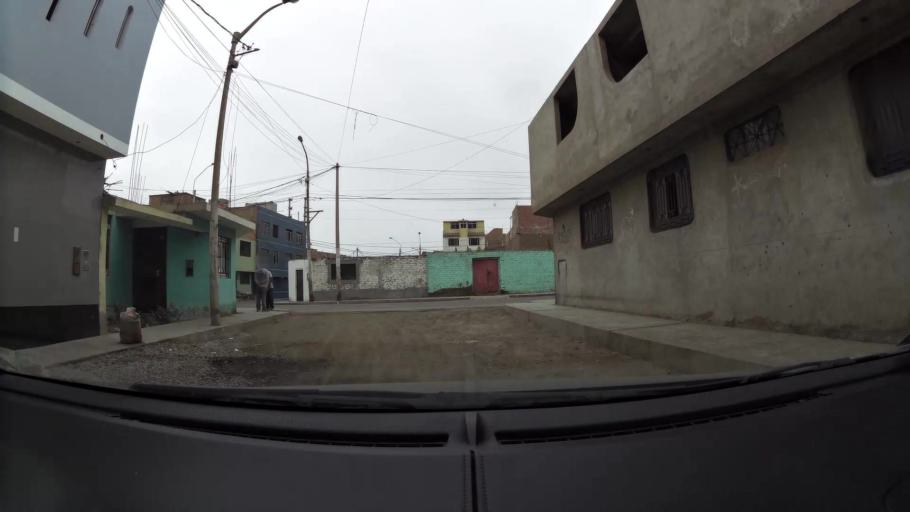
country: PE
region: Lima
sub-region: Barranca
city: Barranca
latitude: -10.7525
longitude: -77.7537
